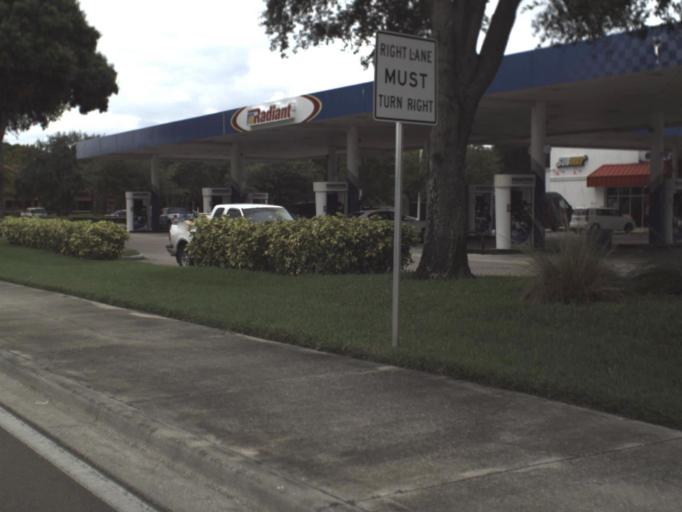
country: US
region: Florida
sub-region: Sarasota County
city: Lake Sarasota
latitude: 27.2990
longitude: -82.4539
